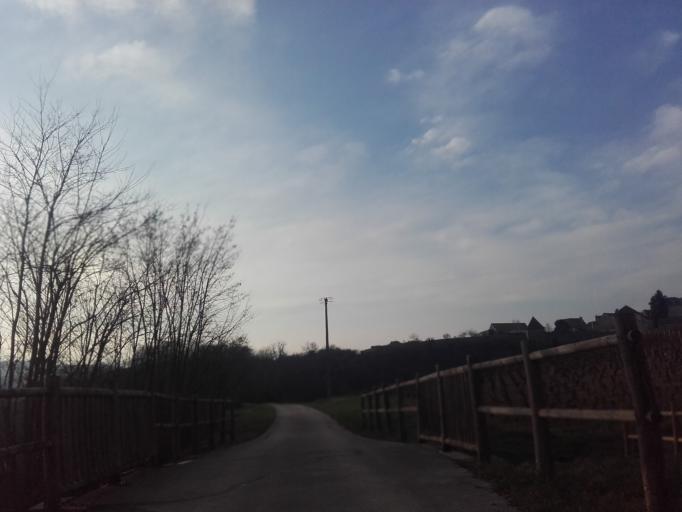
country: FR
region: Bourgogne
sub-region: Departement de la Cote-d'Or
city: Nolay
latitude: 46.9076
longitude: 4.6564
